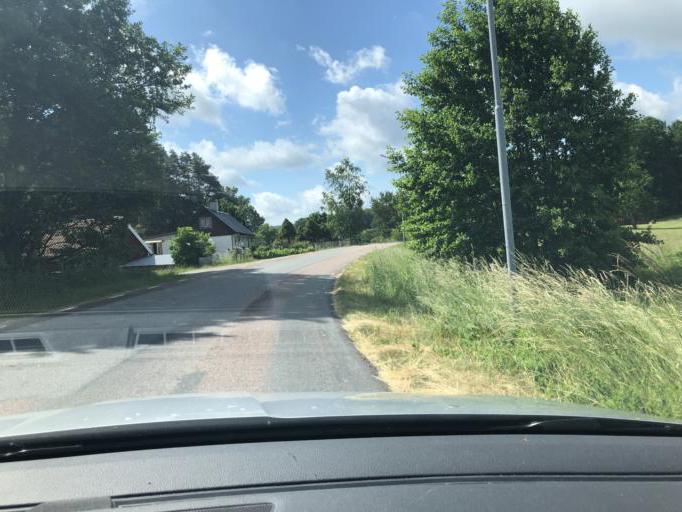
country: SE
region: Blekinge
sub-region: Solvesborgs Kommun
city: Soelvesborg
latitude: 56.1314
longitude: 14.6079
